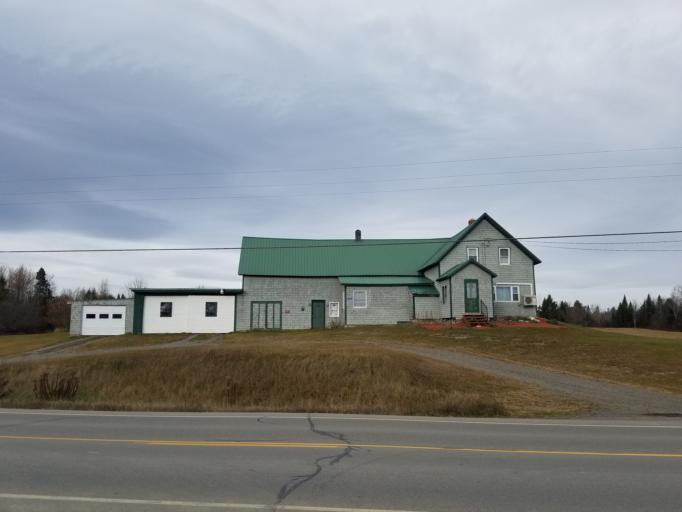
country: US
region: Maine
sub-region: Aroostook County
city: Hodgdon
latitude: 46.1314
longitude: -68.1380
